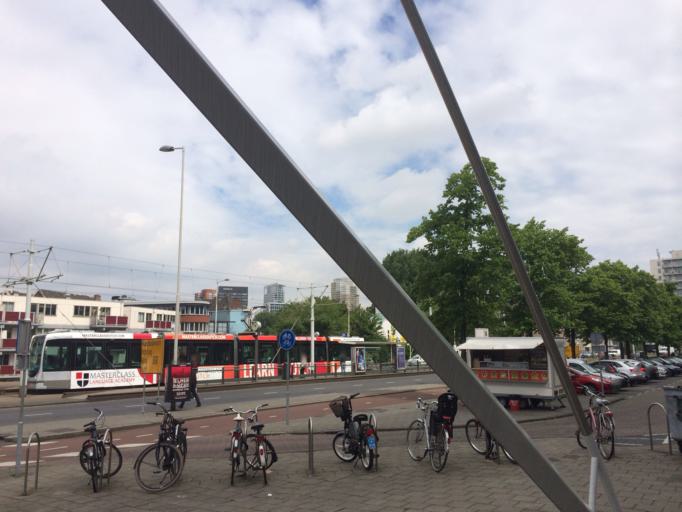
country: NL
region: South Holland
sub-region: Gemeente Rotterdam
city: Rotterdam
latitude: 51.9115
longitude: 4.4782
